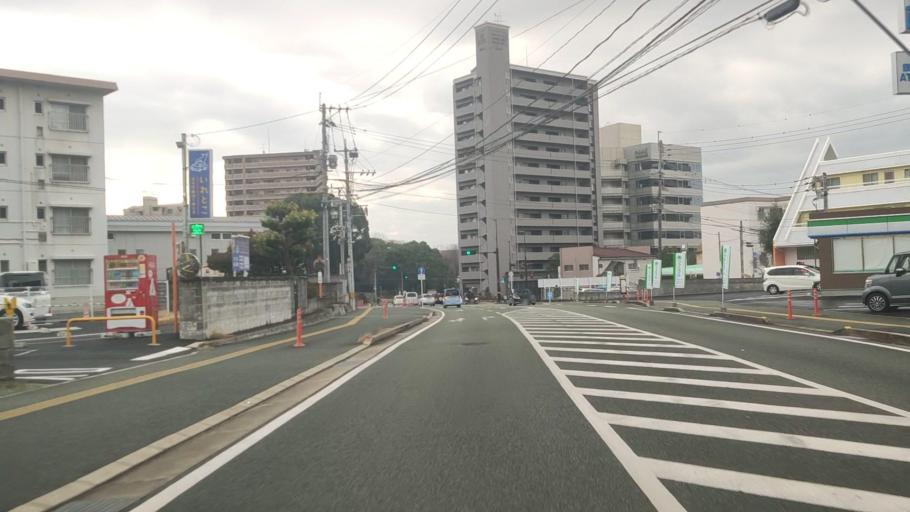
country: JP
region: Kumamoto
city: Kumamoto
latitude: 32.7884
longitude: 130.7384
